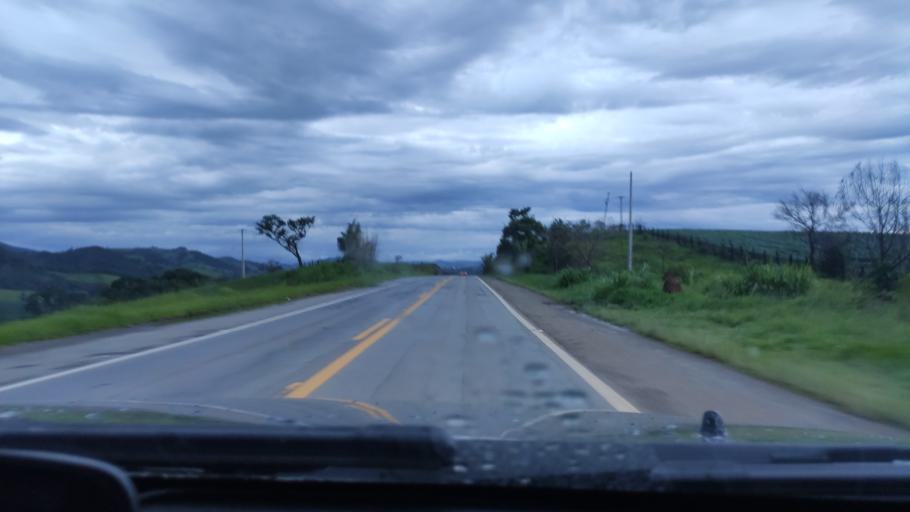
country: BR
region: Sao Paulo
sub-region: Socorro
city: Socorro
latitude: -22.6683
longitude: -46.5565
